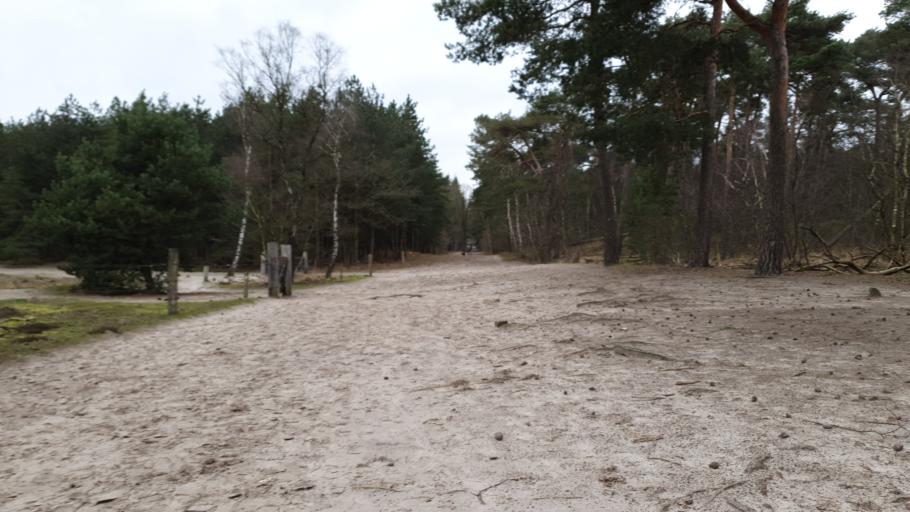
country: NL
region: North Brabant
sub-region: Gemeente Son en Breugel
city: Son
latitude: 51.5167
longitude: 5.4630
